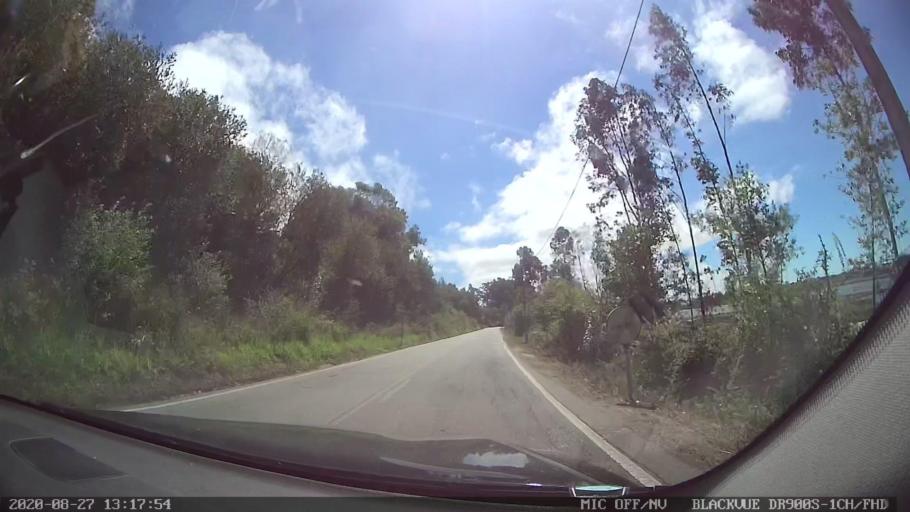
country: PT
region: Aveiro
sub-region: Vagos
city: Vagos
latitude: 40.5782
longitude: -8.6800
